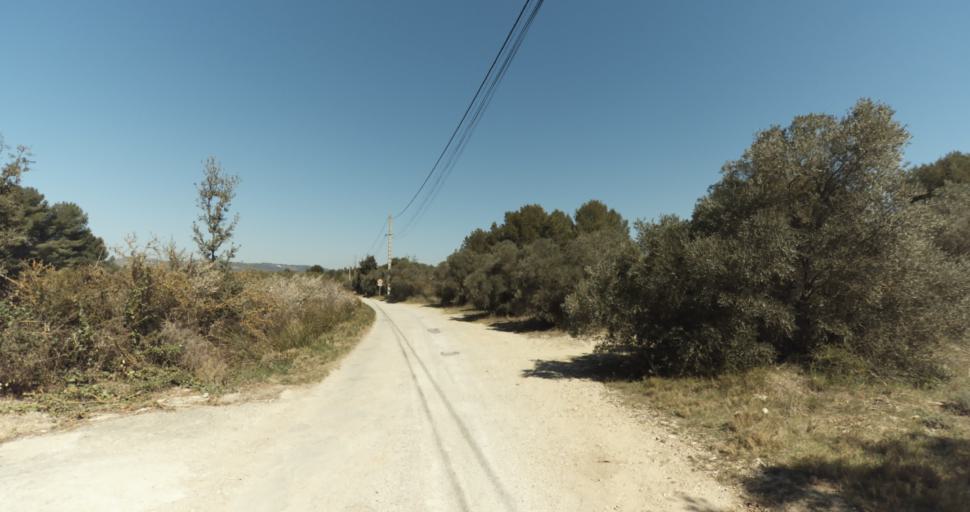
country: FR
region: Provence-Alpes-Cote d'Azur
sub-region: Departement des Bouches-du-Rhone
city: Pelissanne
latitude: 43.6151
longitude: 5.1576
